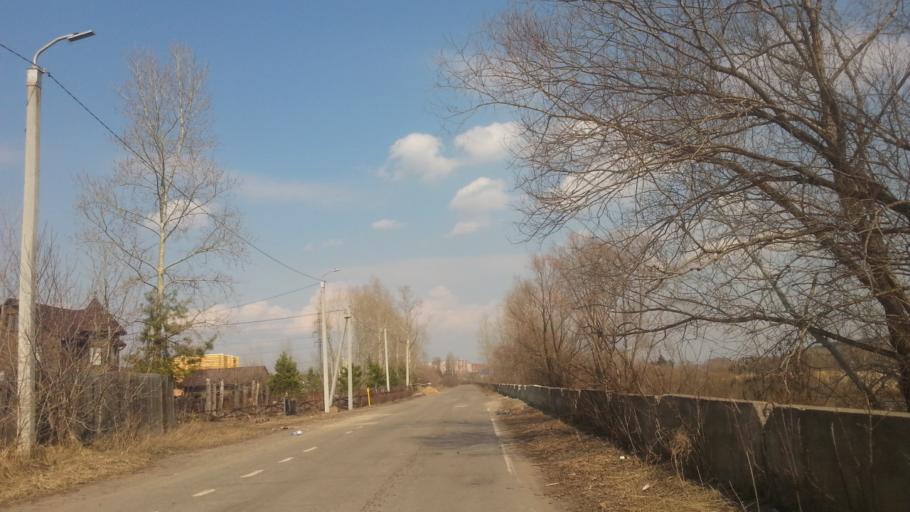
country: RU
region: Altai Krai
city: Yuzhnyy
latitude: 53.3094
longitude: 83.7218
